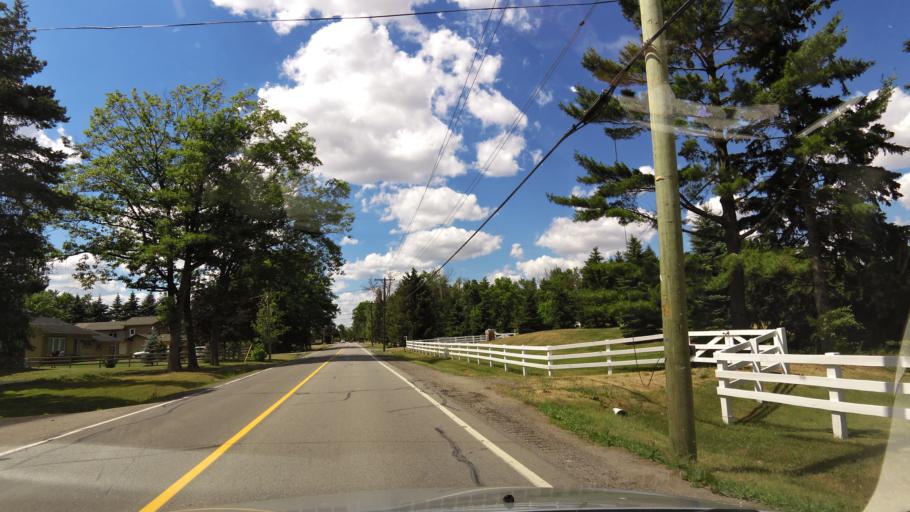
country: CA
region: Ontario
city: Brampton
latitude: 43.6413
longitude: -79.8435
